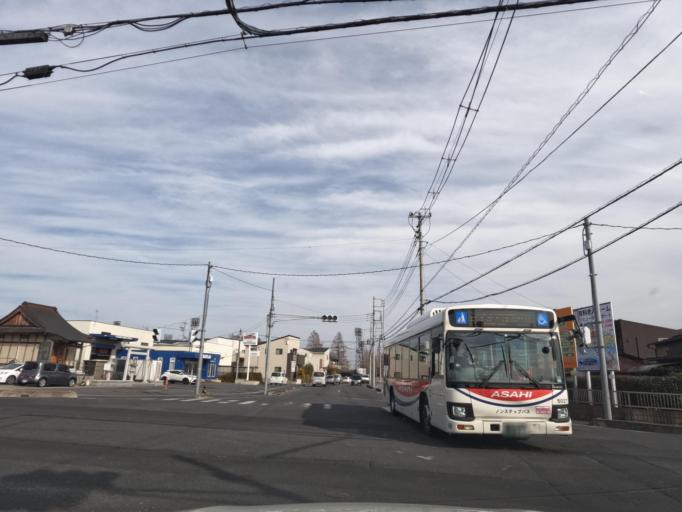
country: JP
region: Saitama
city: Kasukabe
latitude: 35.9622
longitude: 139.7456
